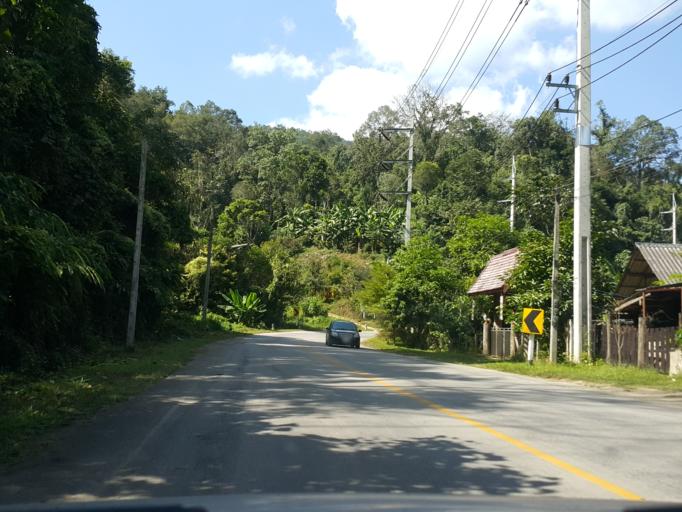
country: TH
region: Chiang Mai
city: Mae Taeng
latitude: 19.1454
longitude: 98.6961
